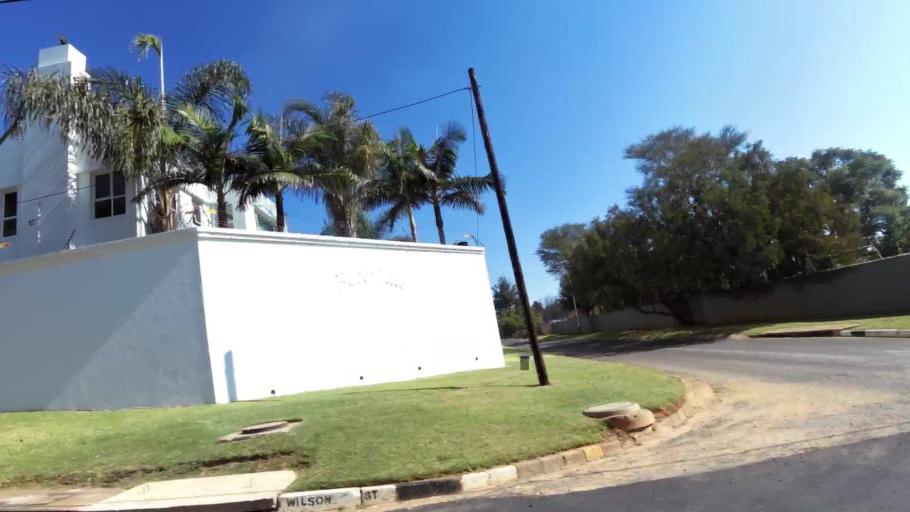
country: ZA
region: Gauteng
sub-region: City of Johannesburg Metropolitan Municipality
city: Roodepoort
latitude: -26.1534
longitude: 27.9453
